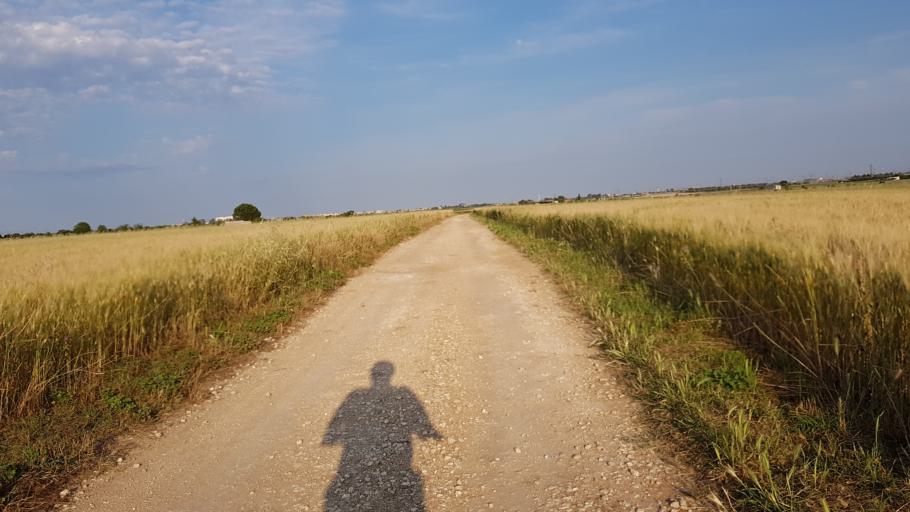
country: IT
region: Apulia
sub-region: Provincia di Brindisi
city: Brindisi
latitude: 40.6256
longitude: 17.8752
